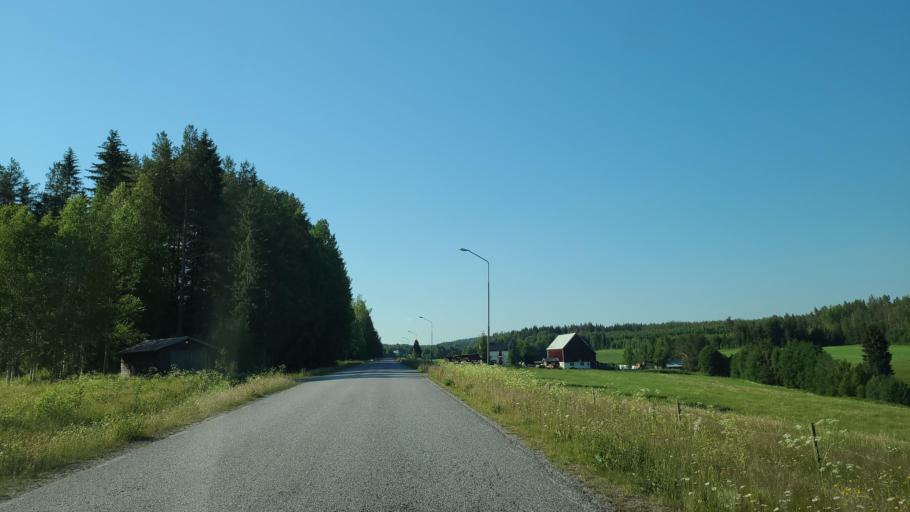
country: SE
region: Vaesterbotten
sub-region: Robertsfors Kommun
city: Robertsfors
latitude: 64.2742
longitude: 20.8089
